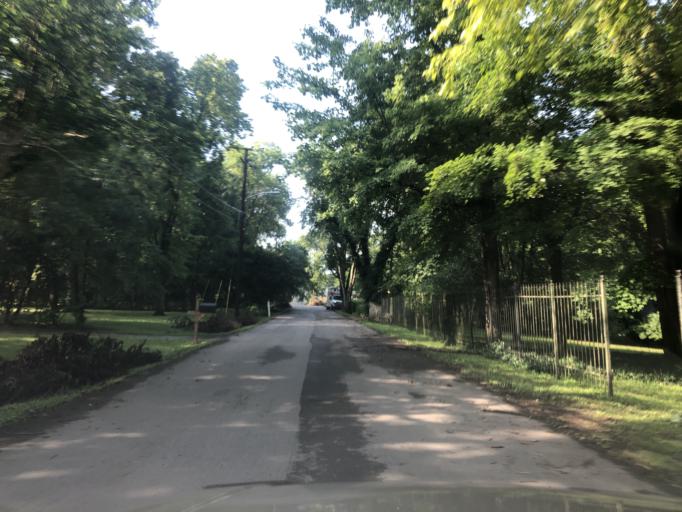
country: US
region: Tennessee
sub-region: Davidson County
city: Lakewood
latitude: 36.2373
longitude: -86.7150
